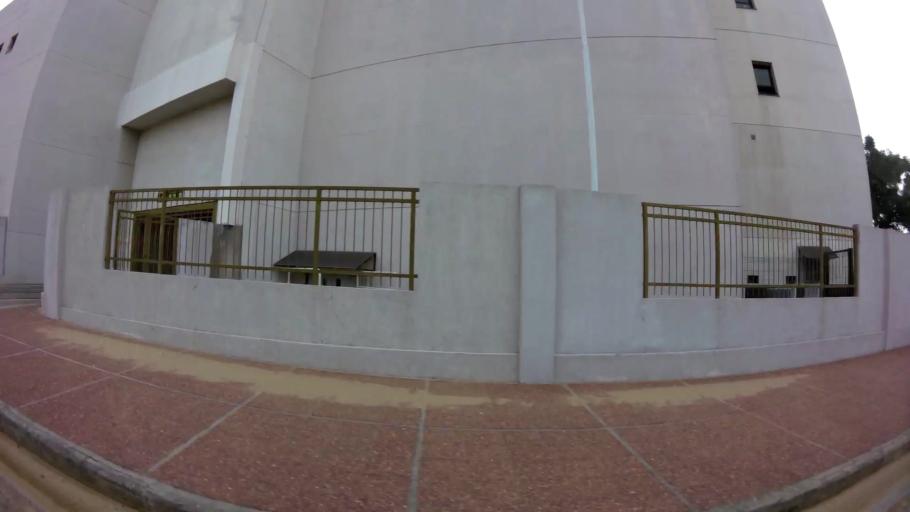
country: PY
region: Central
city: Fernando de la Mora
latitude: -25.3033
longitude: -57.5542
